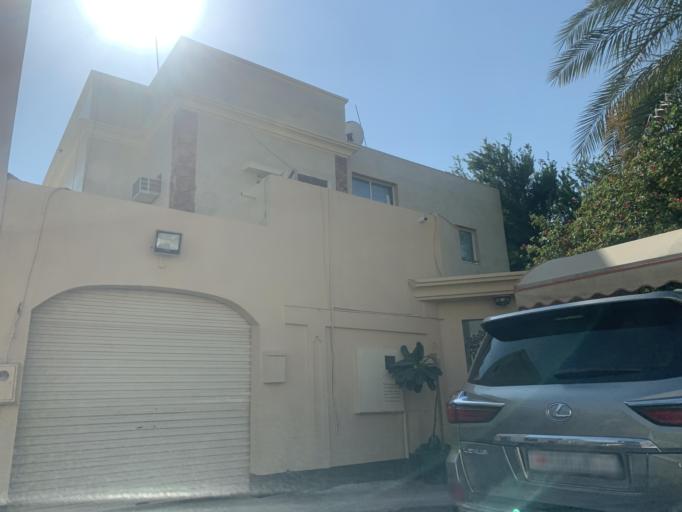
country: BH
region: Central Governorate
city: Madinat Hamad
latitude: 26.1215
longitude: 50.4941
